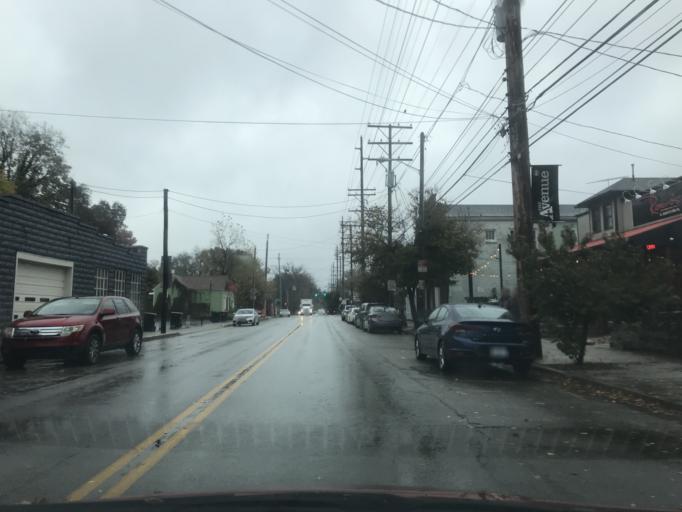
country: US
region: Kentucky
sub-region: Jefferson County
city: Indian Hills
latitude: 38.2535
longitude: -85.7013
